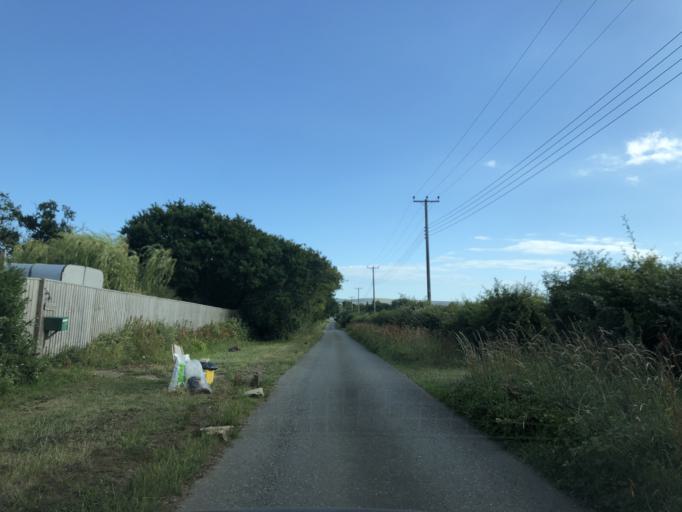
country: GB
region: England
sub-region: Isle of Wight
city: Shalfleet
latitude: 50.7098
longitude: -1.4489
